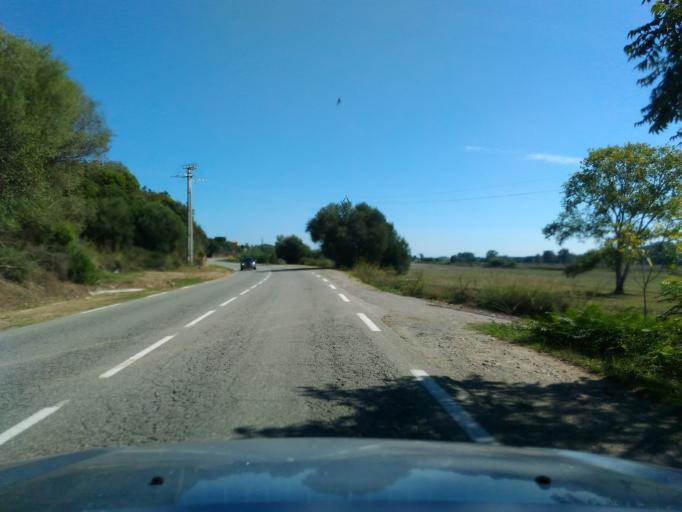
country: FR
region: Corsica
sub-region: Departement de la Haute-Corse
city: Aleria
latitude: 42.1139
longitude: 9.4989
